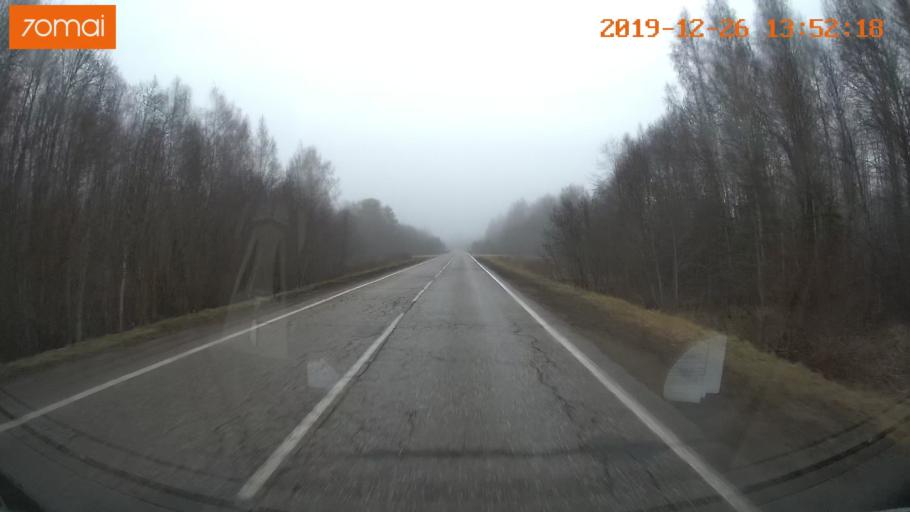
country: RU
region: Jaroslavl
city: Poshekhon'ye
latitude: 58.6337
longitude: 38.6005
